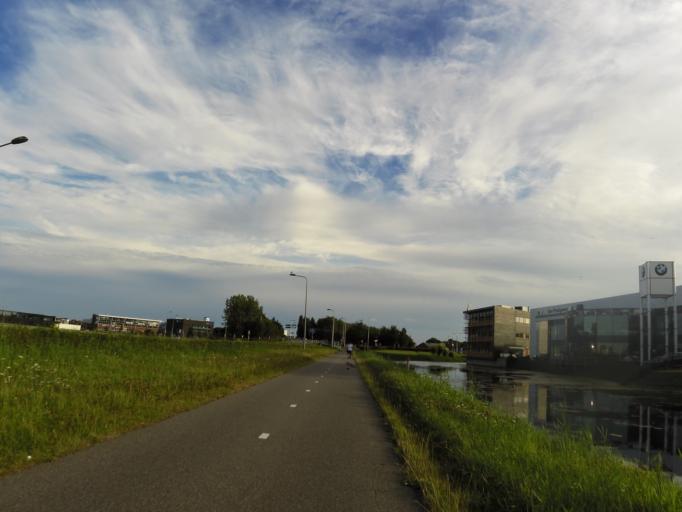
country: NL
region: South Holland
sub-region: Gemeente Noordwijk
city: Noordwijk-Binnen
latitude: 52.2136
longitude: 4.4381
